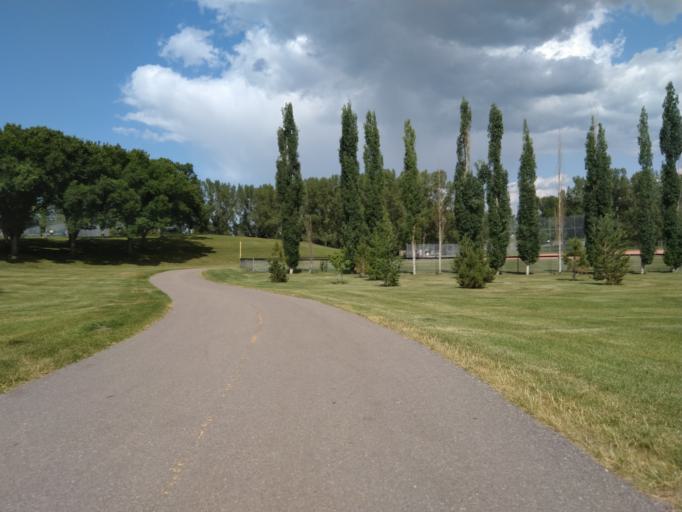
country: CA
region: Alberta
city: Calgary
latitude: 51.0802
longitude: -114.0792
